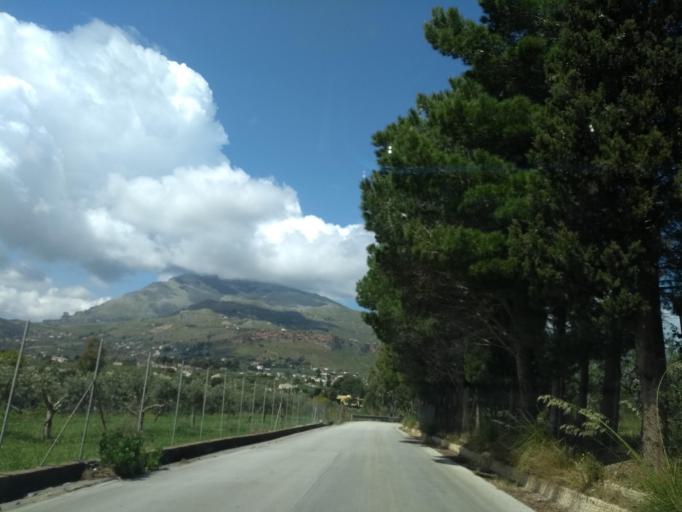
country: IT
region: Sicily
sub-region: Trapani
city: Castellammare del Golfo
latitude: 38.0458
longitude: 12.8441
